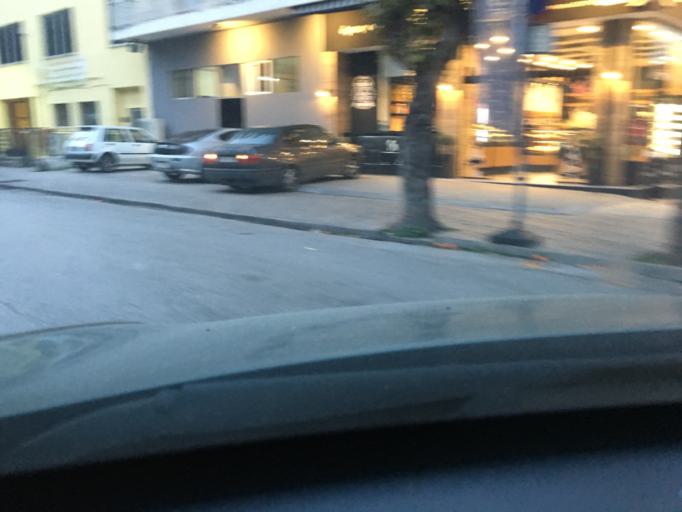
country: GR
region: Attica
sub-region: Nomarchia Athinas
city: Nea Chalkidona
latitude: 38.0323
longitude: 23.7328
